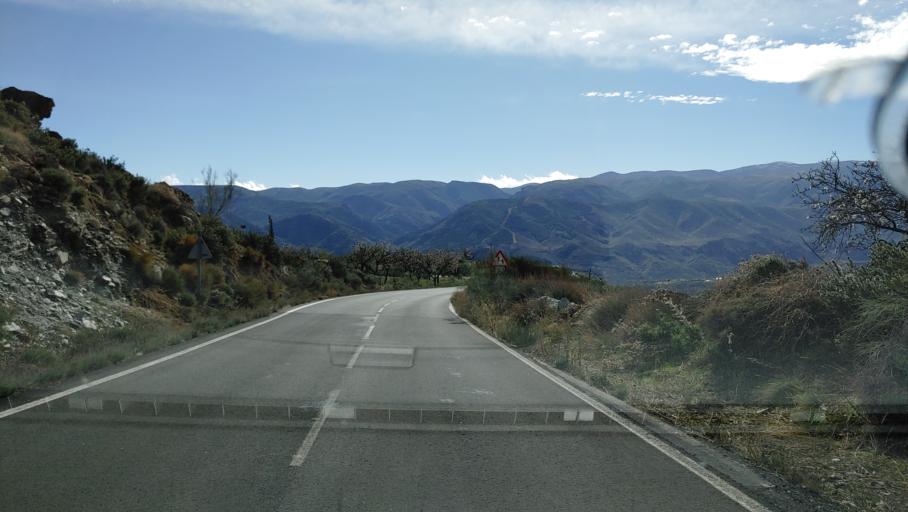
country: ES
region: Andalusia
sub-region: Provincia de Almeria
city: Ohanes
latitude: 37.0280
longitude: -2.7373
